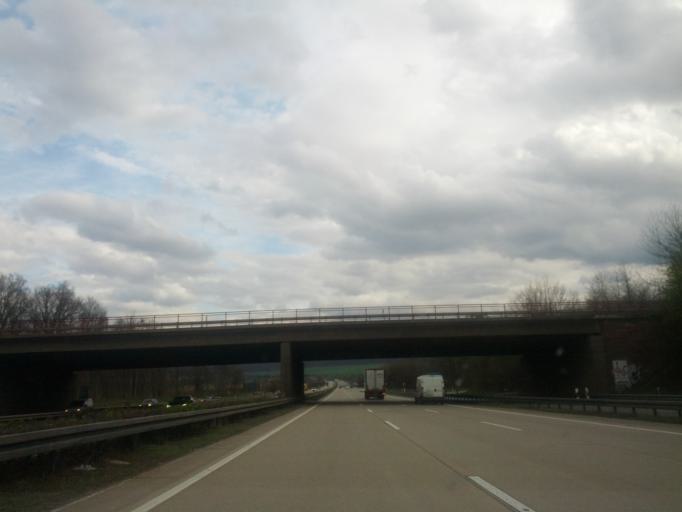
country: DE
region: Lower Saxony
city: Hildesheim
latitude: 52.1616
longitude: 9.9873
